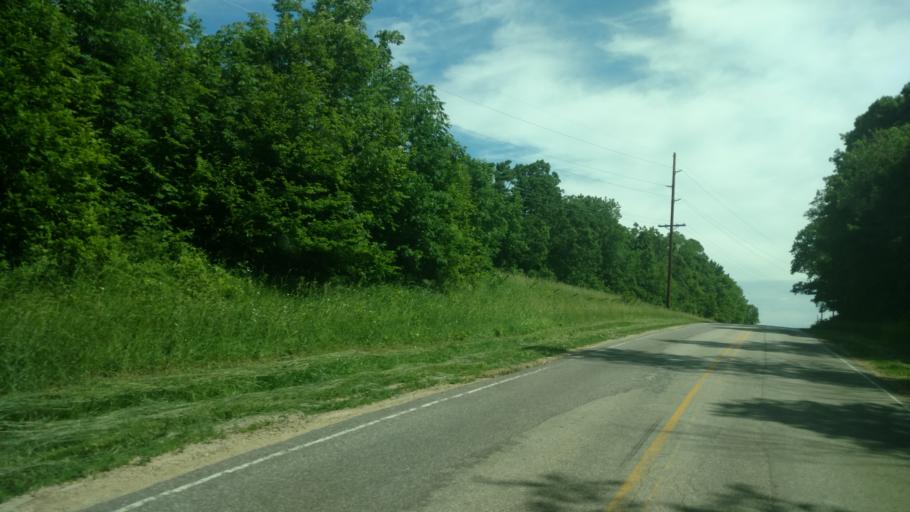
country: US
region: Wisconsin
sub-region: Vernon County
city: Hillsboro
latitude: 43.6737
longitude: -90.4569
